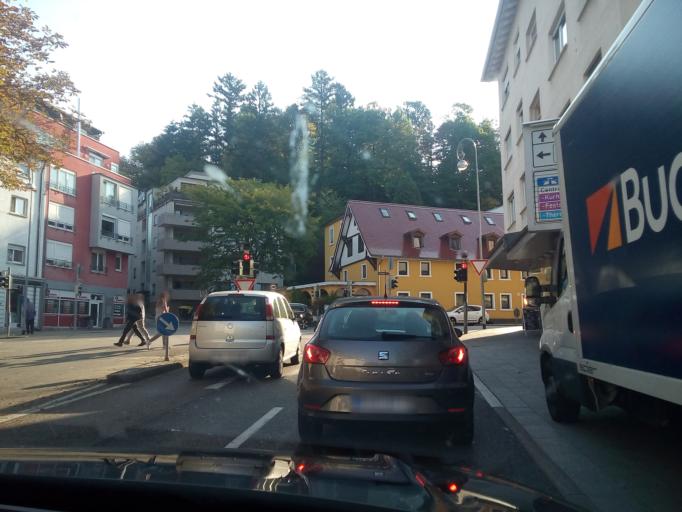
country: DE
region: Baden-Wuerttemberg
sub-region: Karlsruhe Region
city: Baden-Baden
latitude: 48.7550
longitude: 8.2435
